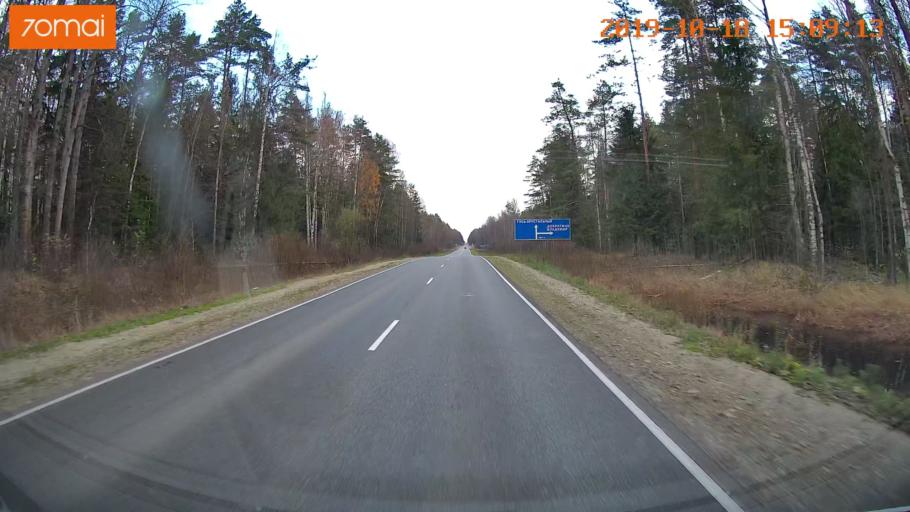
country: RU
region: Vladimir
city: Gus'-Khrustal'nyy
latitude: 55.5632
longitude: 40.6188
